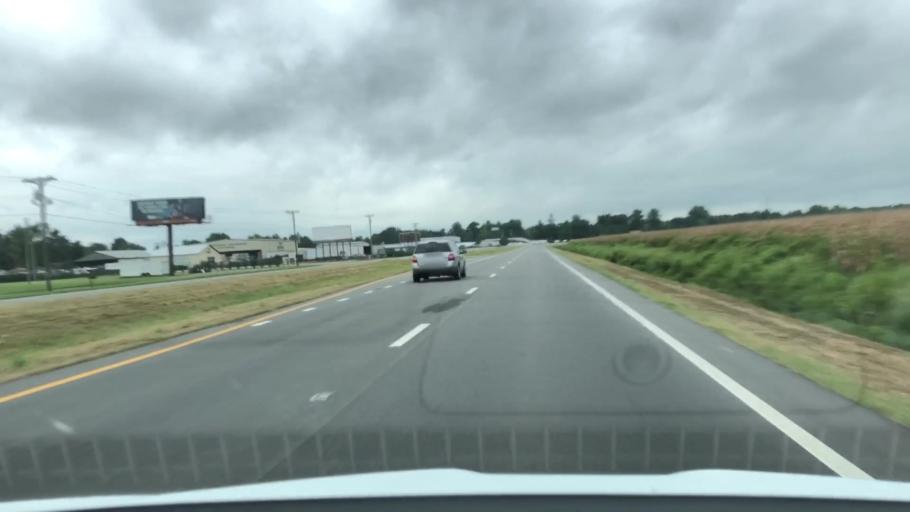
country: US
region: North Carolina
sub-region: Lenoir County
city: La Grange
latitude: 35.2683
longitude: -77.7348
